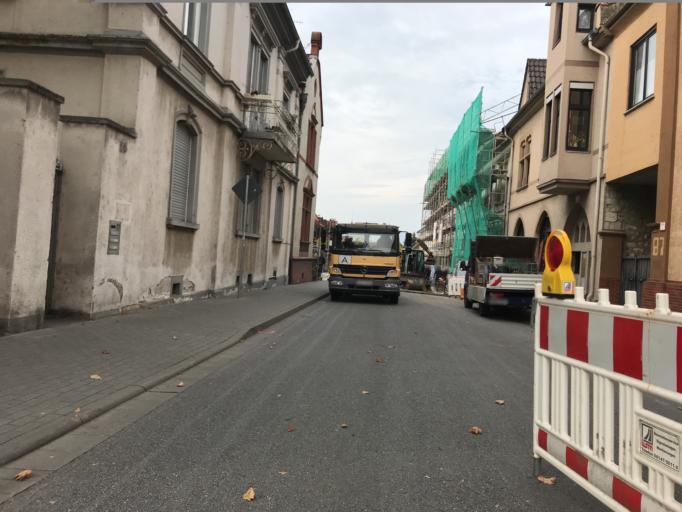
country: DE
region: Rheinland-Pfalz
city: Ingelheim am Rhein
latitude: 49.9681
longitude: 8.0580
